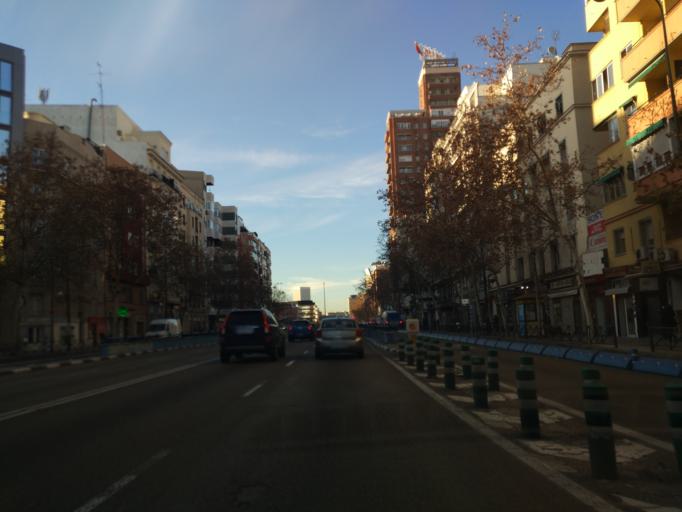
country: ES
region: Madrid
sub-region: Provincia de Madrid
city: Salamanca
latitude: 40.4360
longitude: -3.6758
